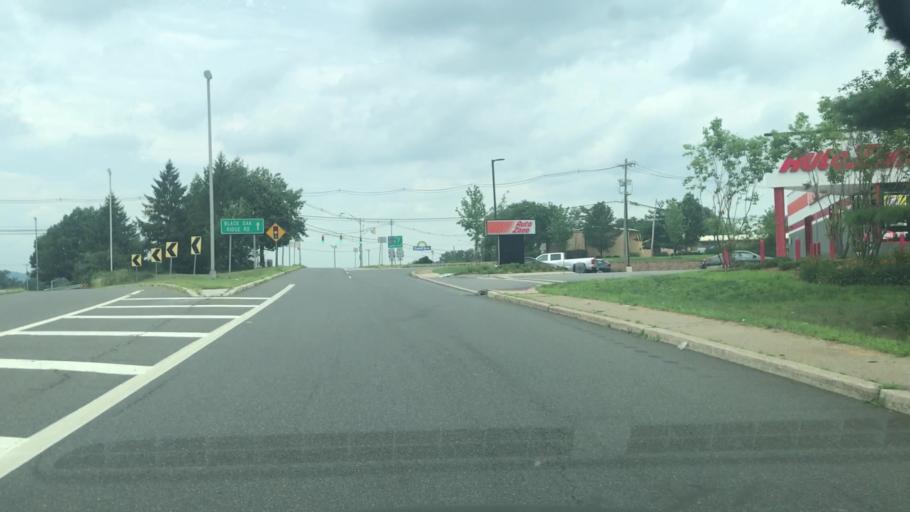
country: US
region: New Jersey
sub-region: Passaic County
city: Wayne
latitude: 40.9459
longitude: -74.2729
